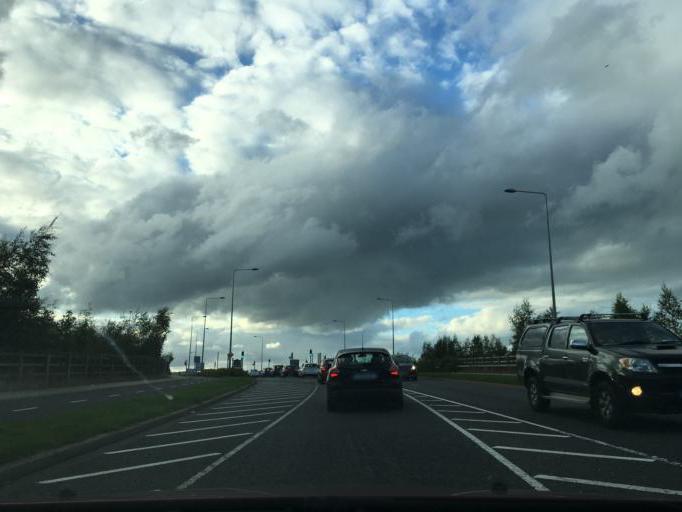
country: IE
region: Leinster
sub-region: Wicklow
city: Rathnew
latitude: 52.9912
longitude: -6.0704
